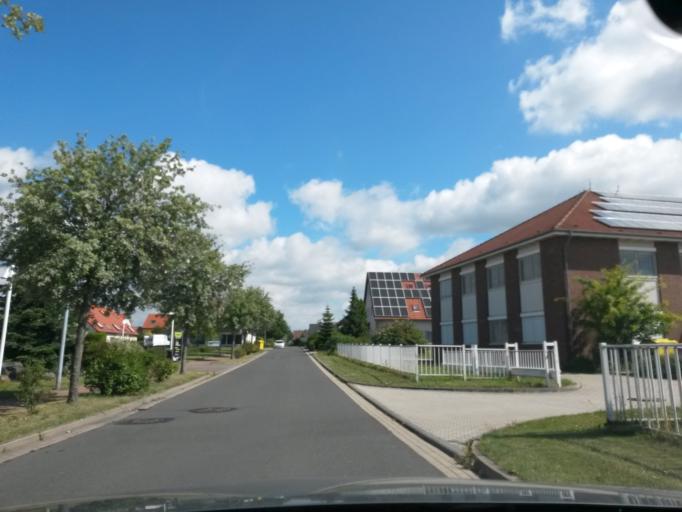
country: DE
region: Thuringia
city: Hermsdorf
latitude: 50.8917
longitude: 11.8676
